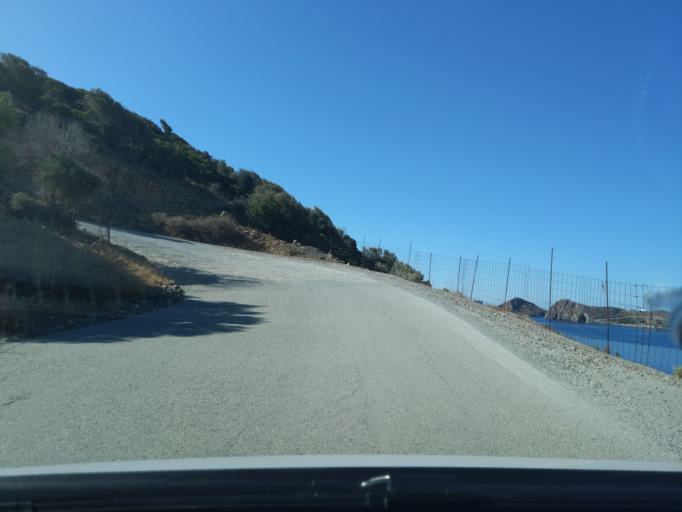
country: GR
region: Crete
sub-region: Nomos Irakleiou
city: Moires
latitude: 34.9383
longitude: 24.8140
